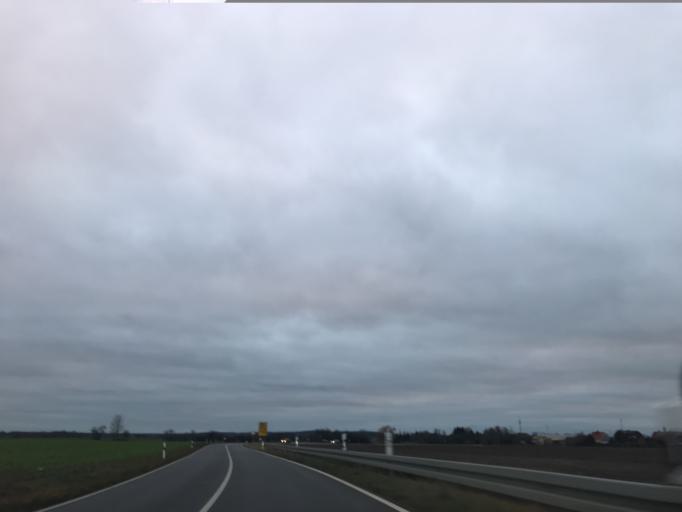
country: DE
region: Brandenburg
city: Wittstock
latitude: 53.1636
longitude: 12.5123
